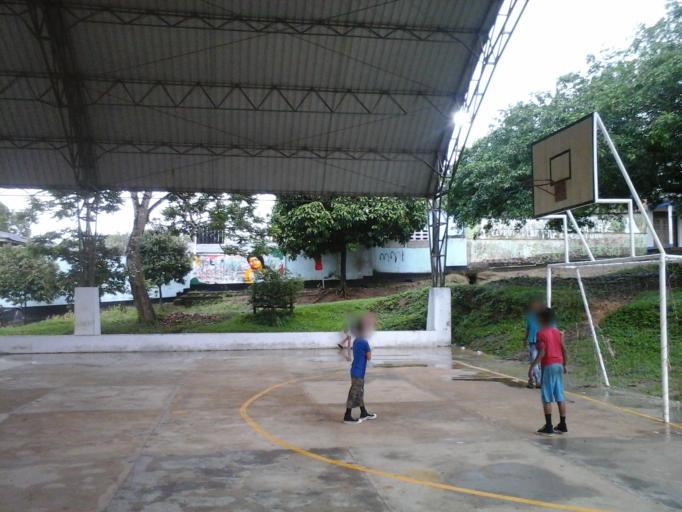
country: CO
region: Caqueta
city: El Doncello
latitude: 1.6122
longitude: -74.9959
